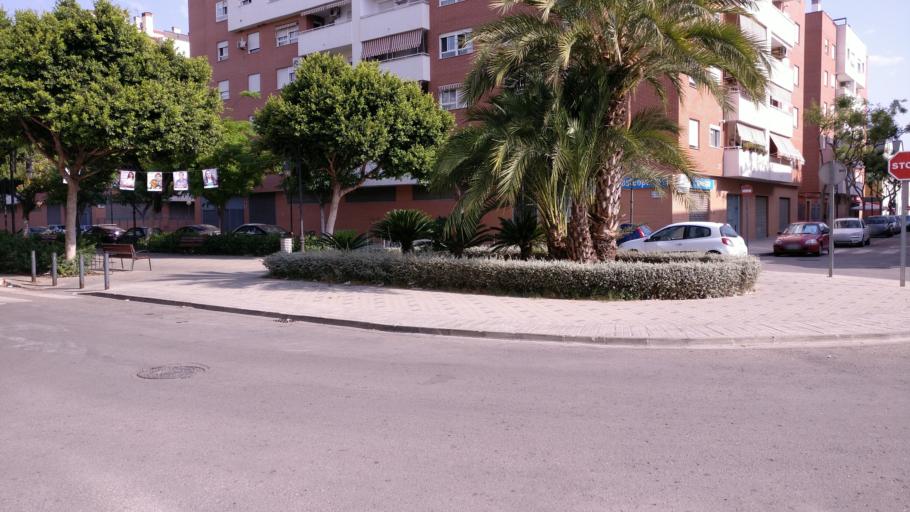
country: ES
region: Valencia
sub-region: Provincia de Valencia
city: Aldaia
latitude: 39.4650
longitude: -0.4569
